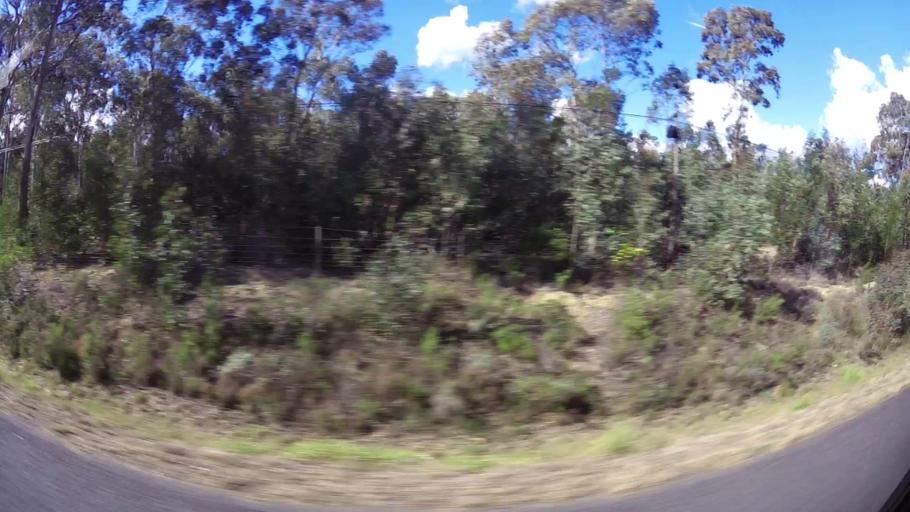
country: ZA
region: Western Cape
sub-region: Overberg District Municipality
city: Swellendam
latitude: -34.0301
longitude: 20.4204
